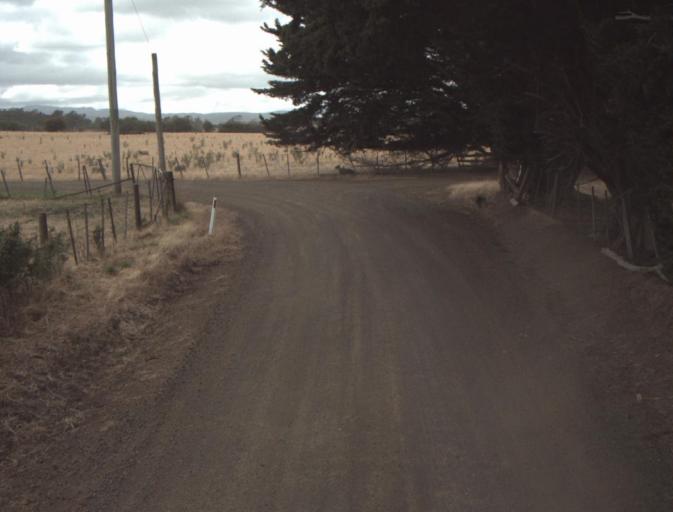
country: AU
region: Tasmania
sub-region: Northern Midlands
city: Evandale
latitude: -41.5233
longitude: 147.2839
